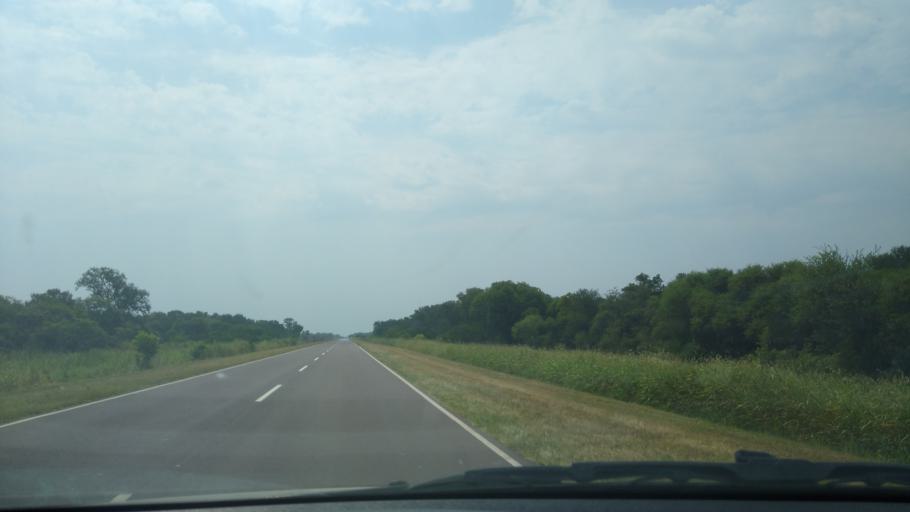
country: AR
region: Chaco
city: La Eduvigis
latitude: -27.0424
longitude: -58.9633
